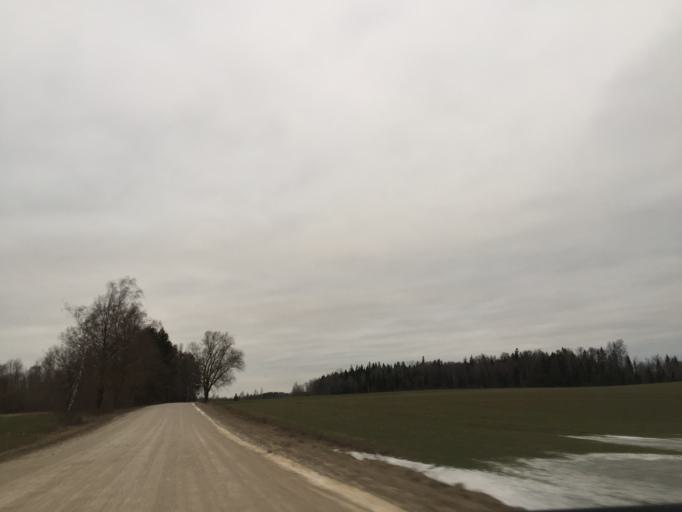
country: LT
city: Zagare
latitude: 56.2828
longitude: 23.2590
